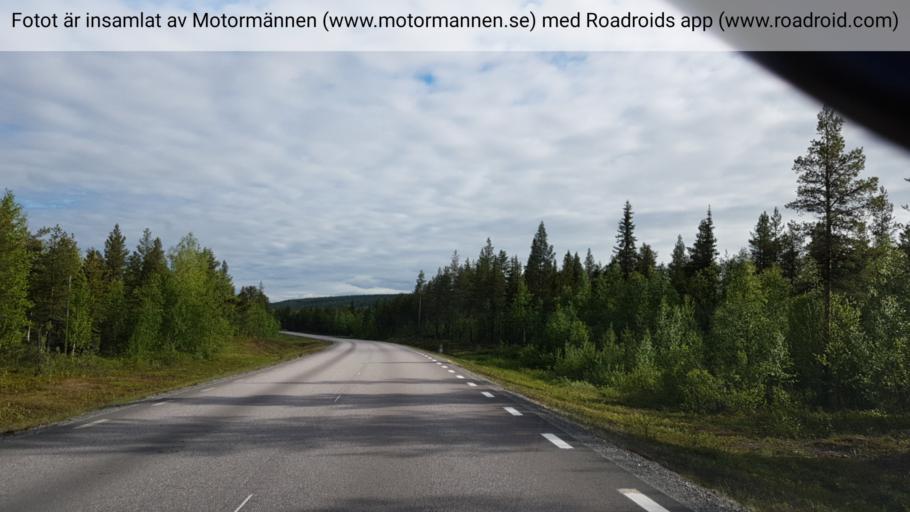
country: SE
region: Norrbotten
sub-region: Gallivare Kommun
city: Malmberget
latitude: 67.4731
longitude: 21.1284
